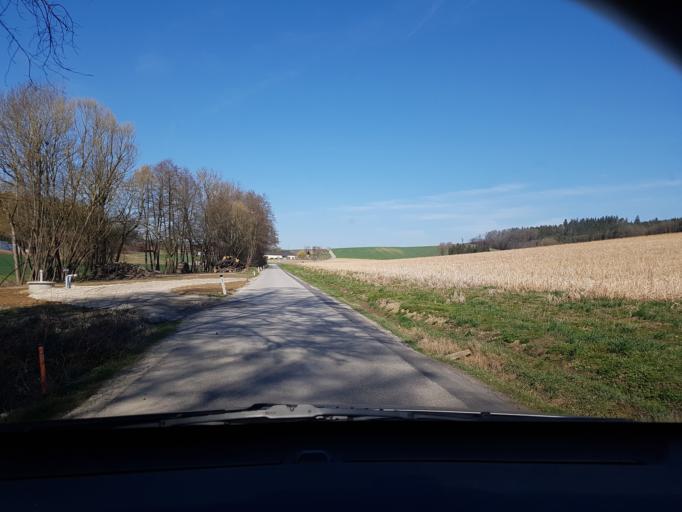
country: AT
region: Upper Austria
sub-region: Politischer Bezirk Linz-Land
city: Ansfelden
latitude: 48.1889
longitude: 14.3291
